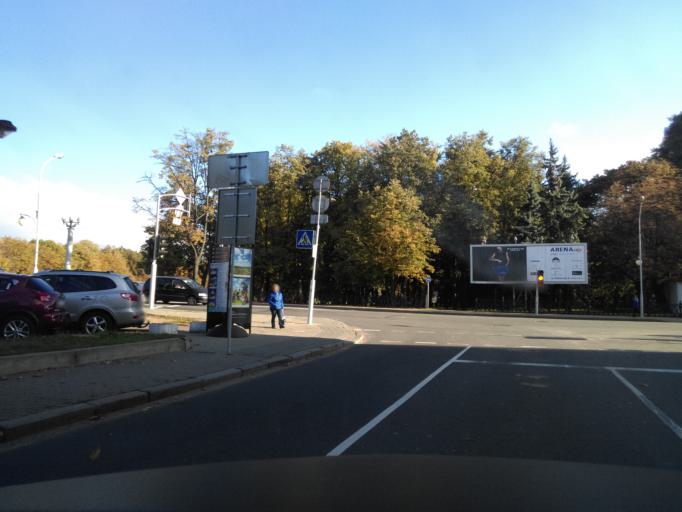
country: BY
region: Minsk
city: Minsk
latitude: 53.9059
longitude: 27.5637
